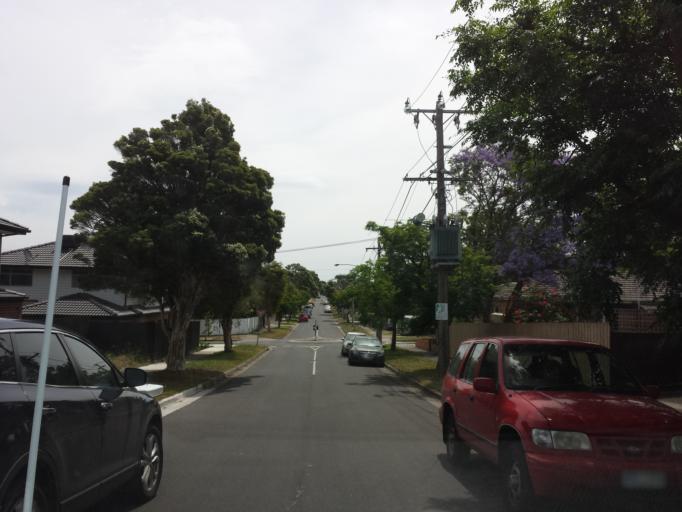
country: AU
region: Victoria
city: Highett
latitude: -37.9363
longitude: 145.0684
